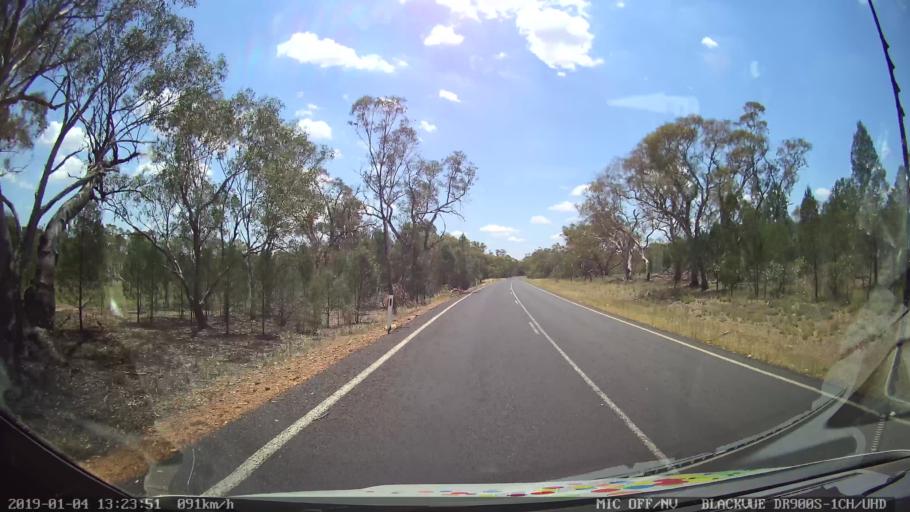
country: AU
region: New South Wales
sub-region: Parkes
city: Peak Hill
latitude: -32.7132
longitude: 148.5516
